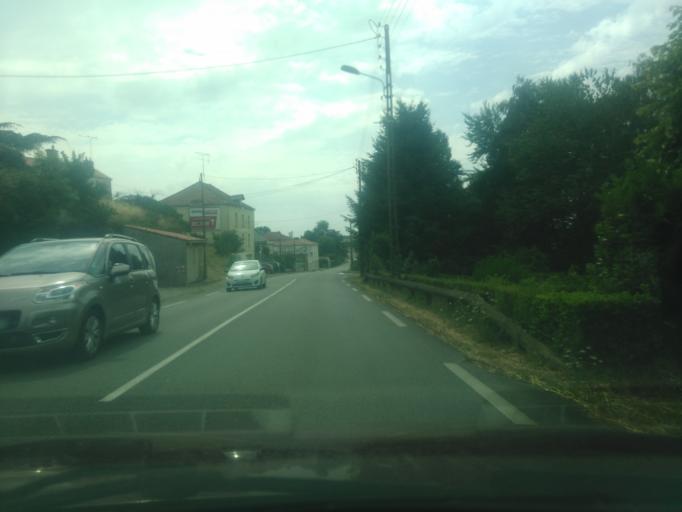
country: FR
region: Pays de la Loire
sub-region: Departement de la Vendee
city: Saint-Pierre-du-Chemin
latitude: 46.6521
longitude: -0.6802
